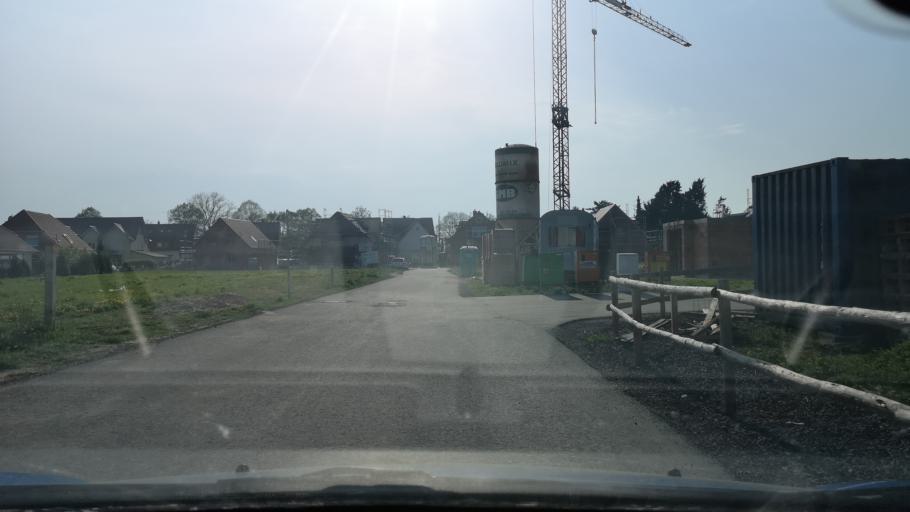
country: DE
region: Lower Saxony
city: Langenhagen
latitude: 52.4451
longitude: 9.6711
